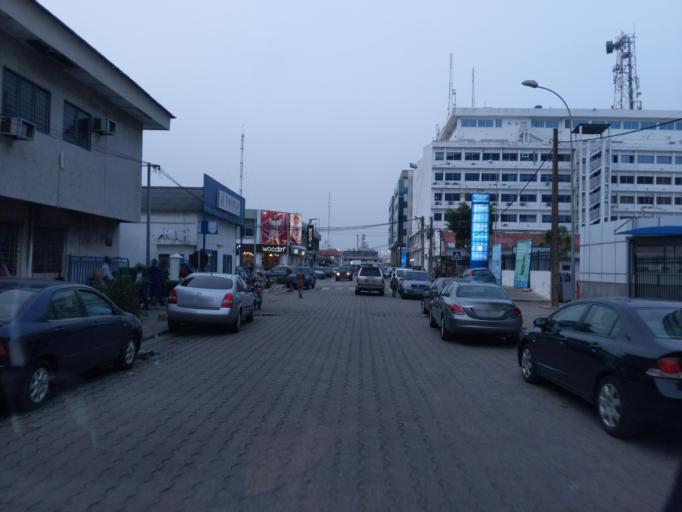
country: BJ
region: Littoral
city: Cotonou
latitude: 6.3531
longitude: 2.4376
